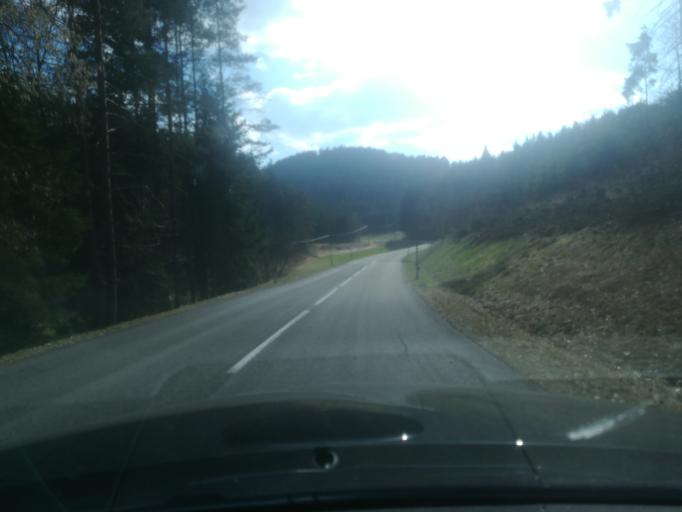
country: AT
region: Lower Austria
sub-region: Politischer Bezirk Zwettl
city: Langschlag
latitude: 48.4642
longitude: 14.7137
